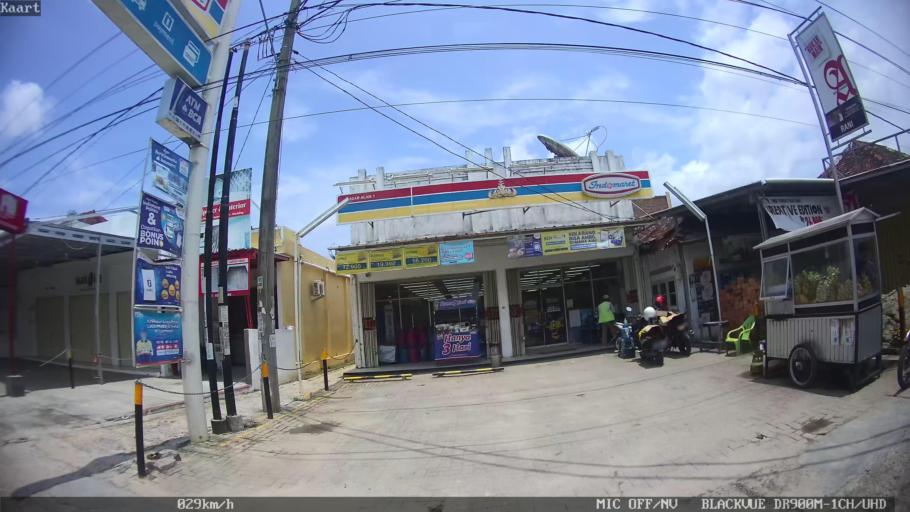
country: ID
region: Lampung
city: Kedaton
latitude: -5.3855
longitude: 105.2535
